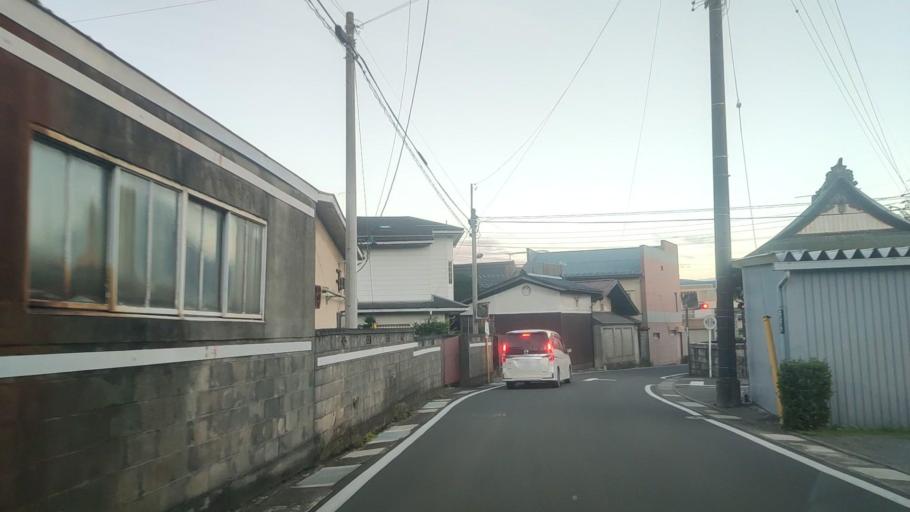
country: JP
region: Nagano
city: Okaya
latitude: 36.0690
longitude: 138.0556
